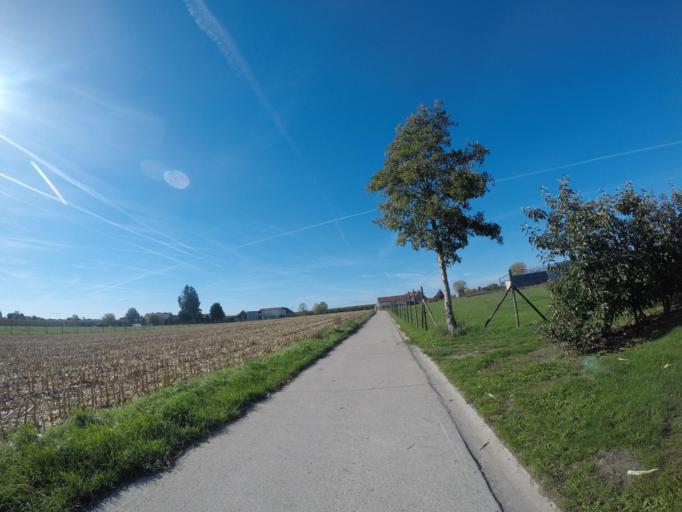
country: BE
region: Flanders
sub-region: Provincie Limburg
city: Alken
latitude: 50.8833
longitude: 5.2503
